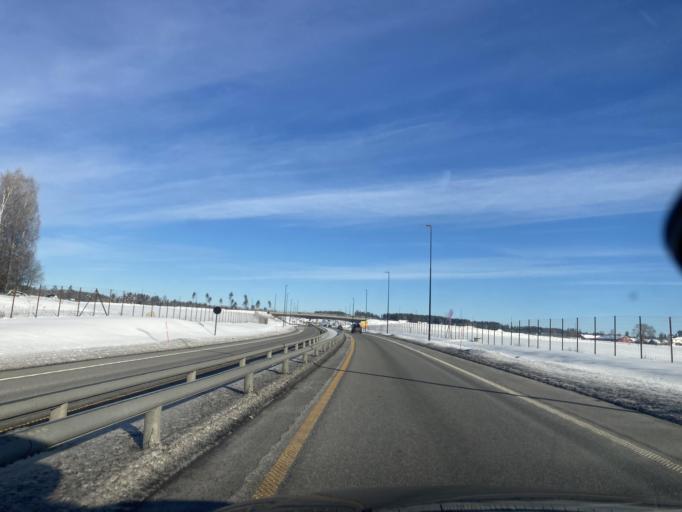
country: NO
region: Hedmark
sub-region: Loten
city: Loten
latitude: 60.8234
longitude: 11.2922
